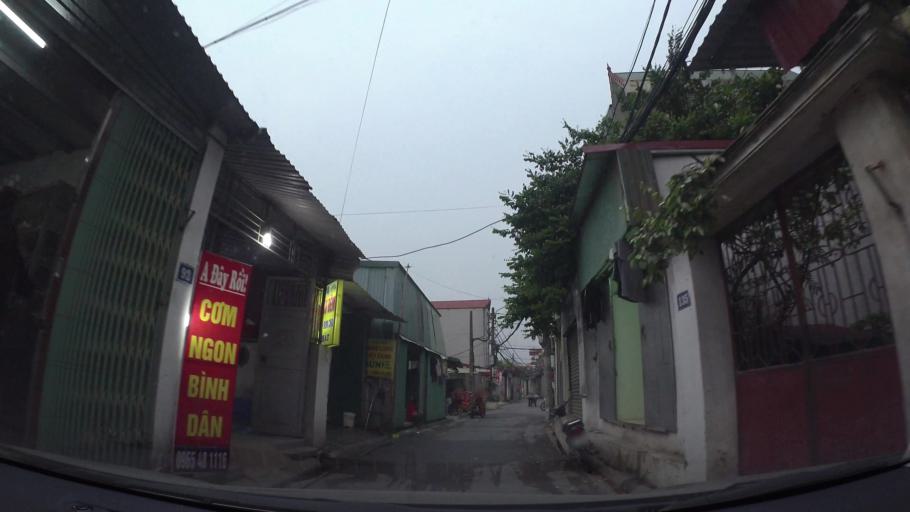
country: VN
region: Ha Noi
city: Trau Quy
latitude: 21.0419
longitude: 105.9018
